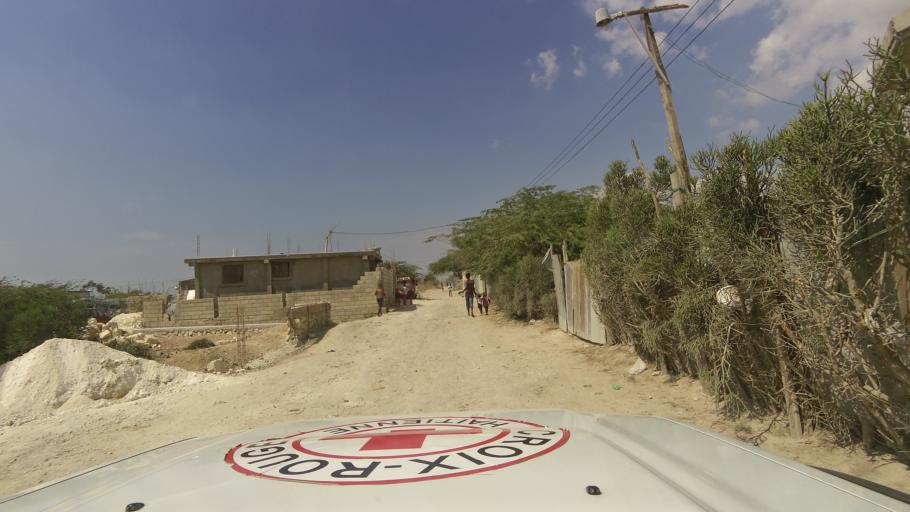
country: HT
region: Ouest
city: Croix des Bouquets
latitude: 18.6475
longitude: -72.2618
